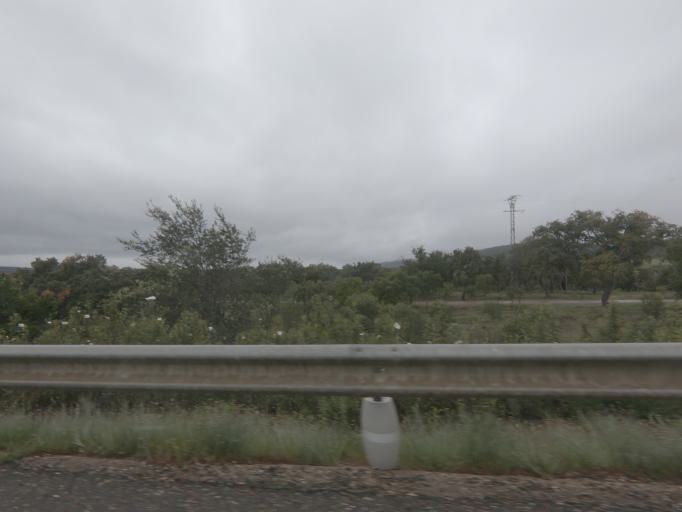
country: ES
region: Extremadura
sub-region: Provincia de Badajoz
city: Puebla de Obando
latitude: 39.1596
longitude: -6.6426
